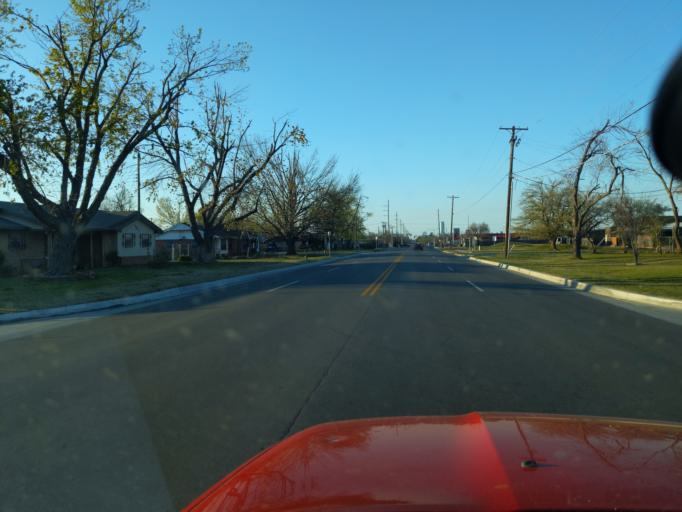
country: US
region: Oklahoma
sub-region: Oklahoma County
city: Oklahoma City
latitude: 35.4037
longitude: -97.5213
